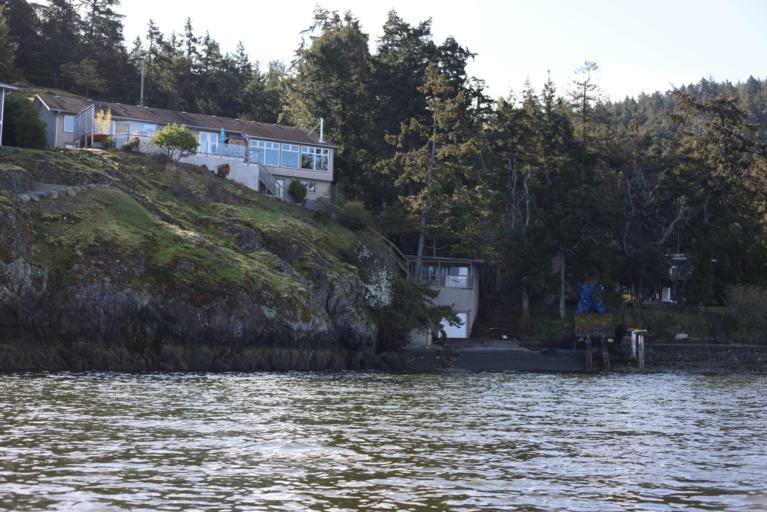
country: CA
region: British Columbia
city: North Saanich
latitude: 48.5756
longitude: -123.4893
